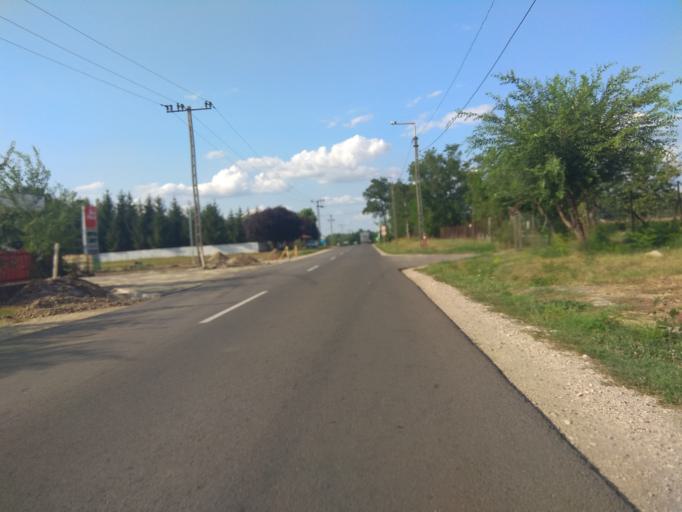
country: HU
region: Borsod-Abauj-Zemplen
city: Mezocsat
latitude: 47.8350
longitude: 20.9004
